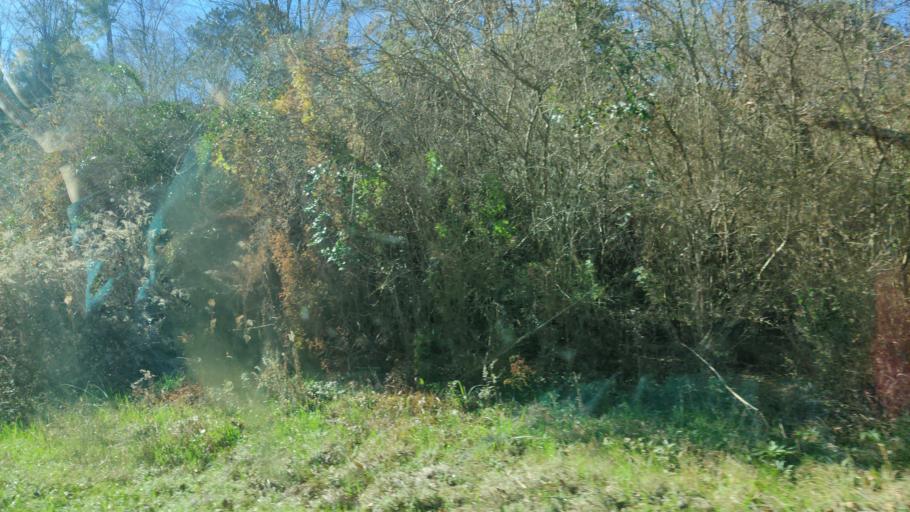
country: US
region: Mississippi
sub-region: Jones County
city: Ellisville
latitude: 31.5506
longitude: -89.3292
